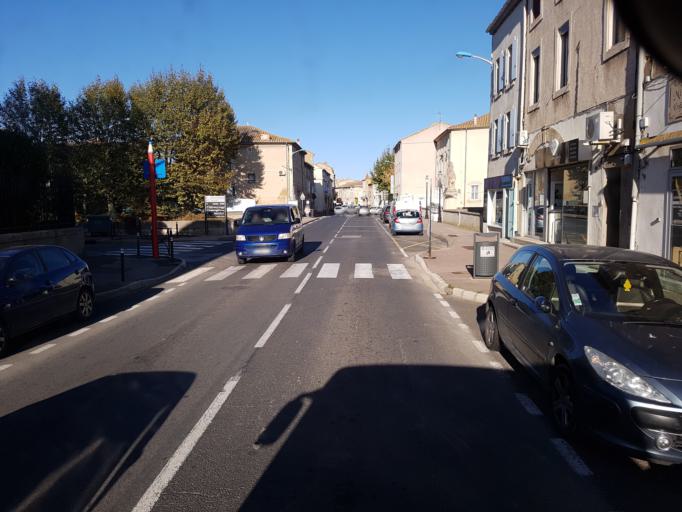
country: FR
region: Languedoc-Roussillon
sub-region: Departement de l'Aude
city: Coursan
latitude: 43.2326
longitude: 3.0554
